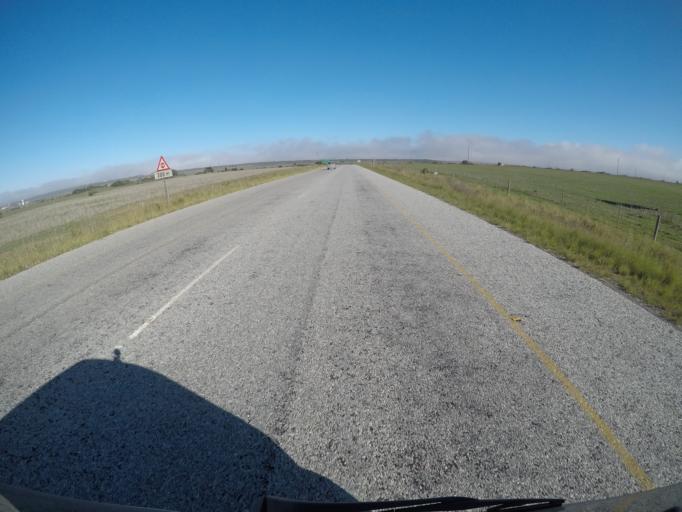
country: ZA
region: Western Cape
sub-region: Eden District Municipality
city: Mossel Bay
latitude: -34.1781
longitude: 22.0167
